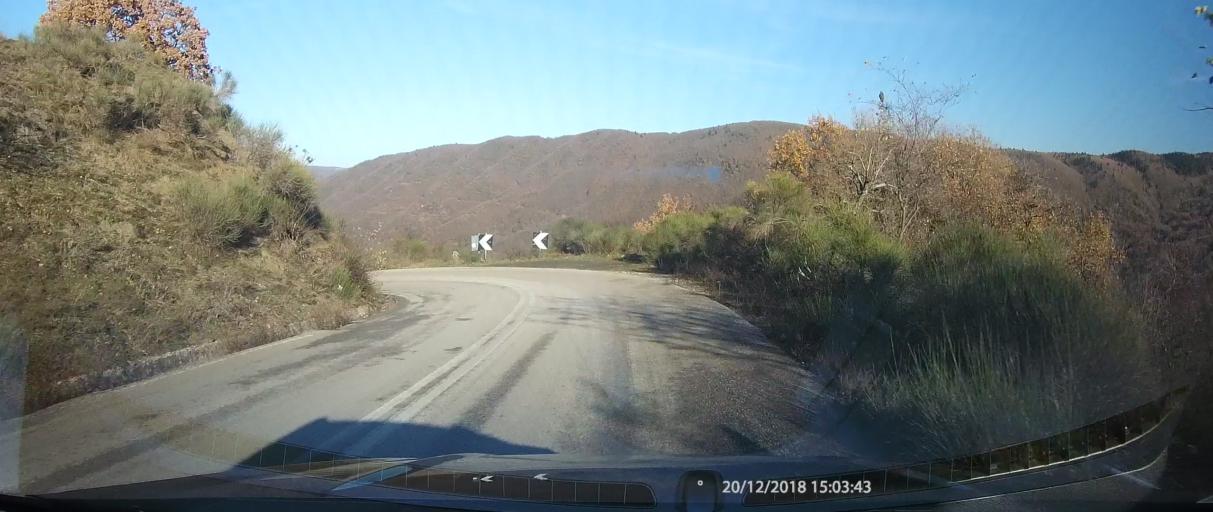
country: GR
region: Central Greece
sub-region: Nomos Evrytanias
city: Karpenisi
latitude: 38.9116
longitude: 21.9240
